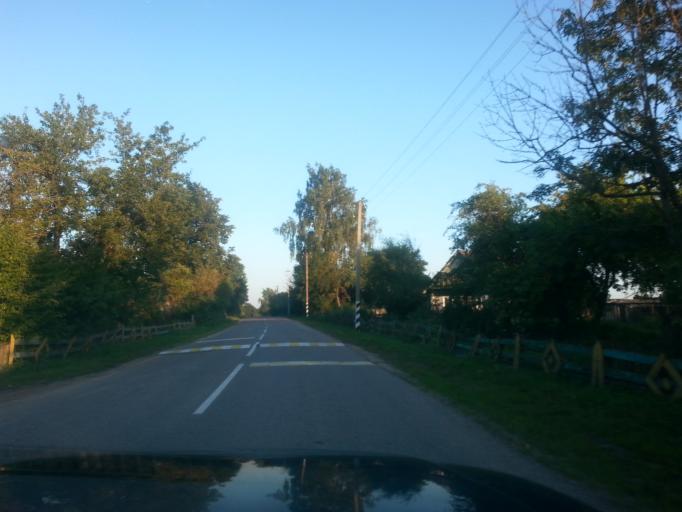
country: BY
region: Minsk
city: Narach
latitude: 55.0584
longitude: 26.6083
